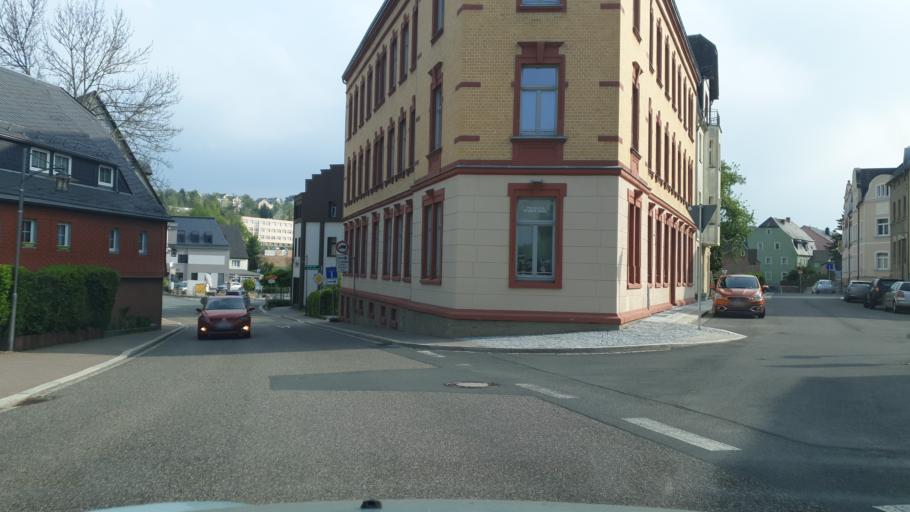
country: DE
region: Saxony
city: Stollberg
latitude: 50.7112
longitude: 12.7819
